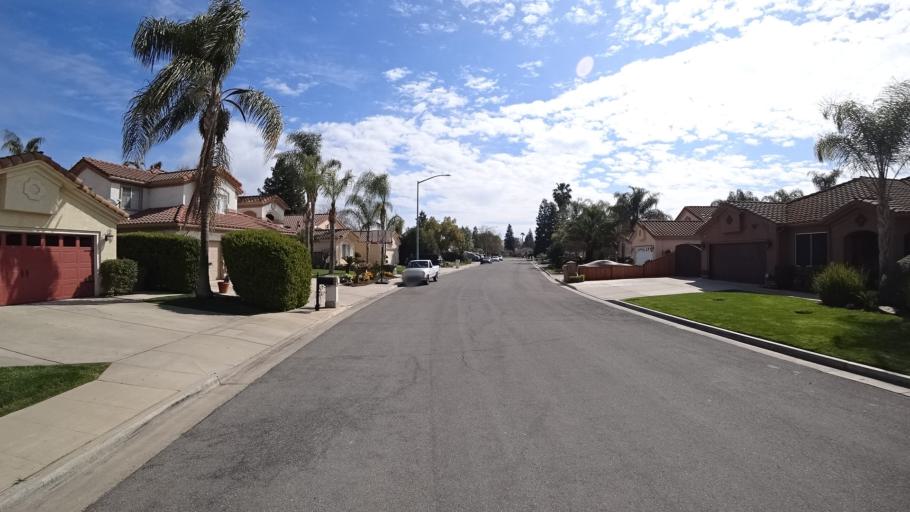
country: US
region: California
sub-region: Fresno County
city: Biola
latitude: 36.8461
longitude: -119.8920
